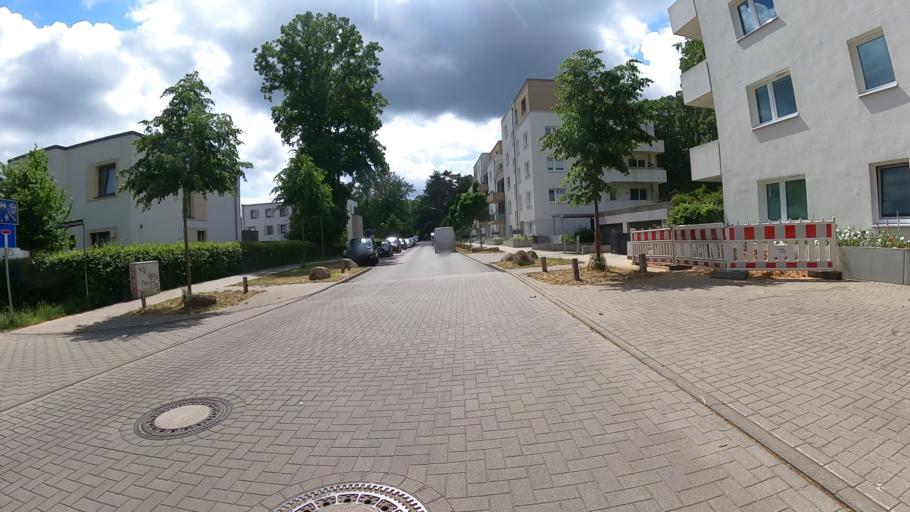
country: DE
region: Hamburg
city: Langenhorn
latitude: 53.6702
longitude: 10.0102
